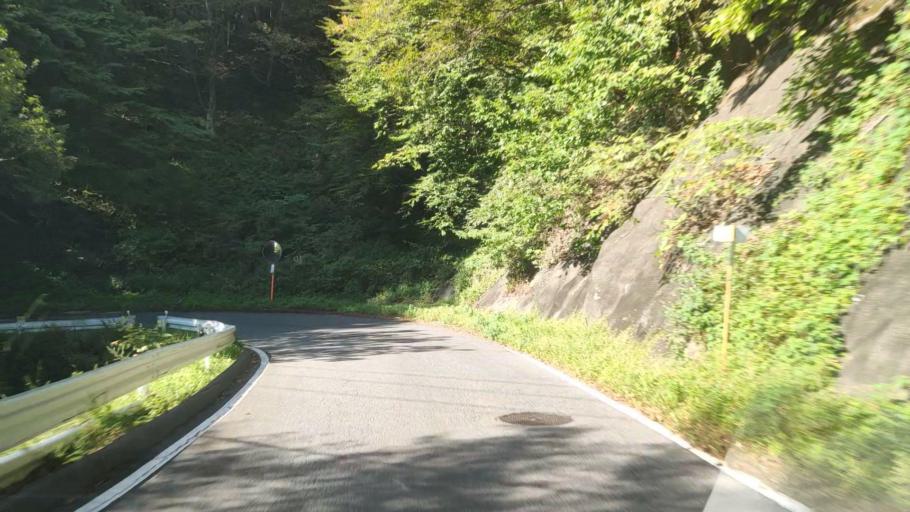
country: JP
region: Gunma
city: Nakanojomachi
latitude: 36.6012
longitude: 138.6835
